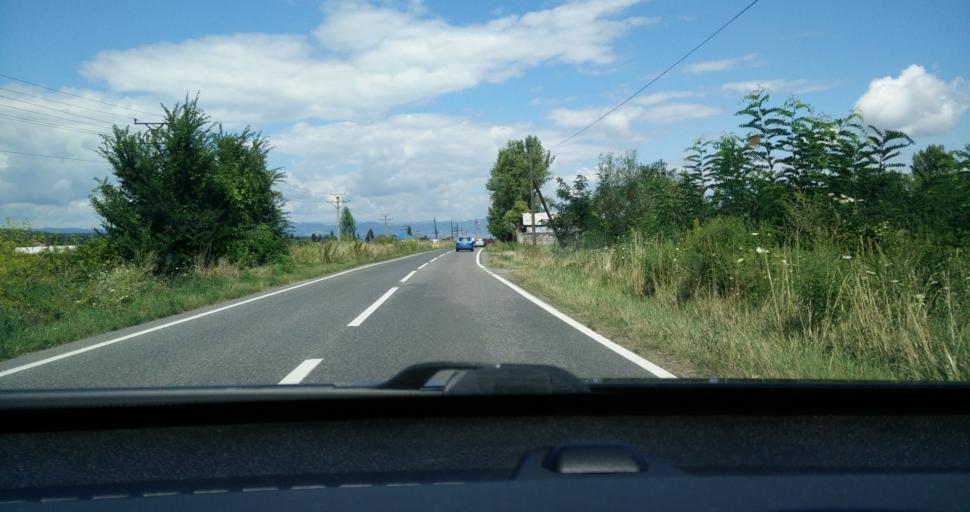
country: RO
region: Alba
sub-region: Comuna Sasciori
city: Sebesel
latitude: 45.9025
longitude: 23.5576
